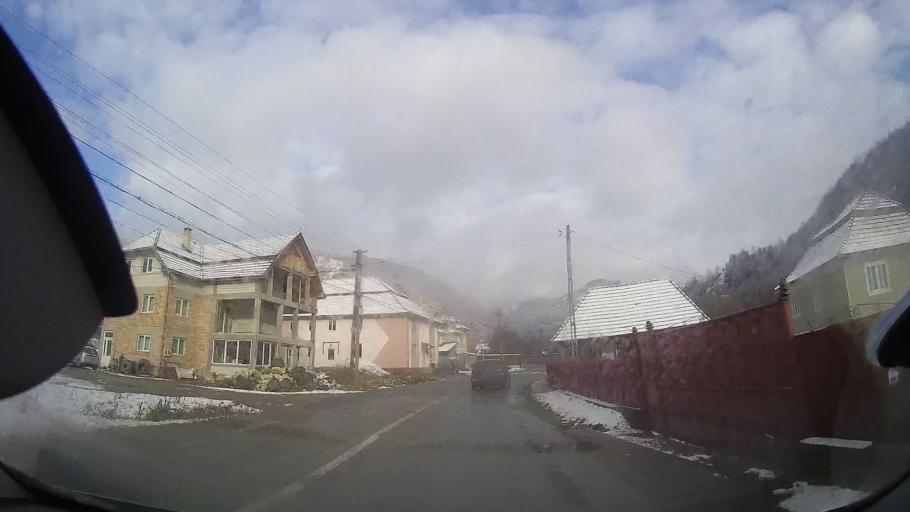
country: RO
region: Alba
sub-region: Oras Baia de Aries
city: Baia de Aries
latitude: 46.3924
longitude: 23.2999
